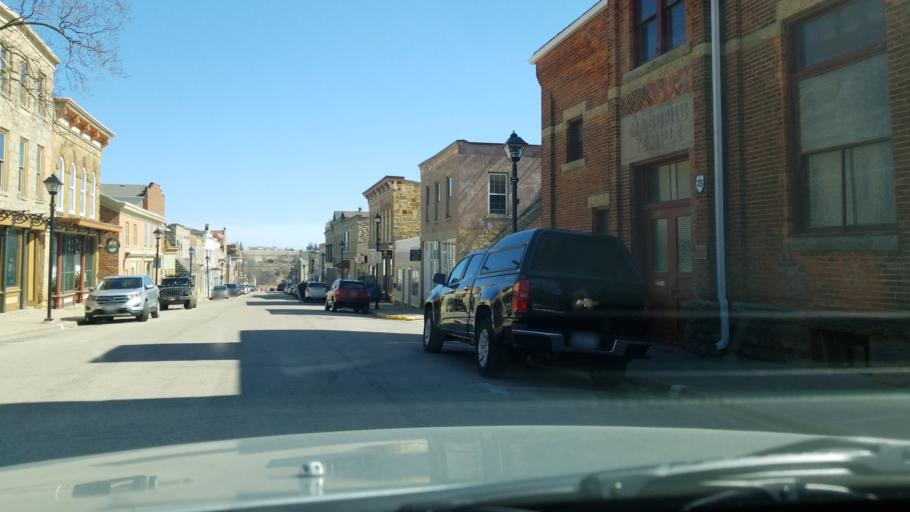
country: US
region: Wisconsin
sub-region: Iowa County
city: Mineral Point
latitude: 42.8606
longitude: -90.1819
